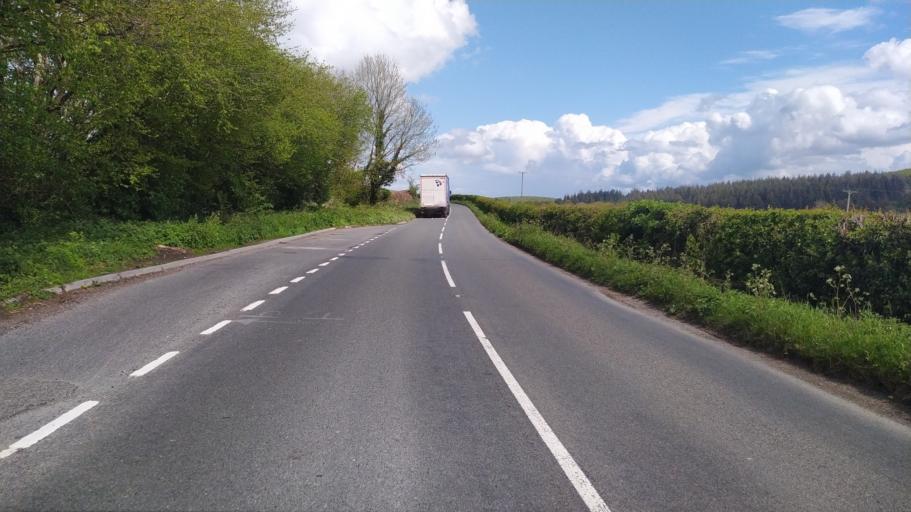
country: GB
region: England
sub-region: Wiltshire
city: Kilmington
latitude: 51.1611
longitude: -2.2931
